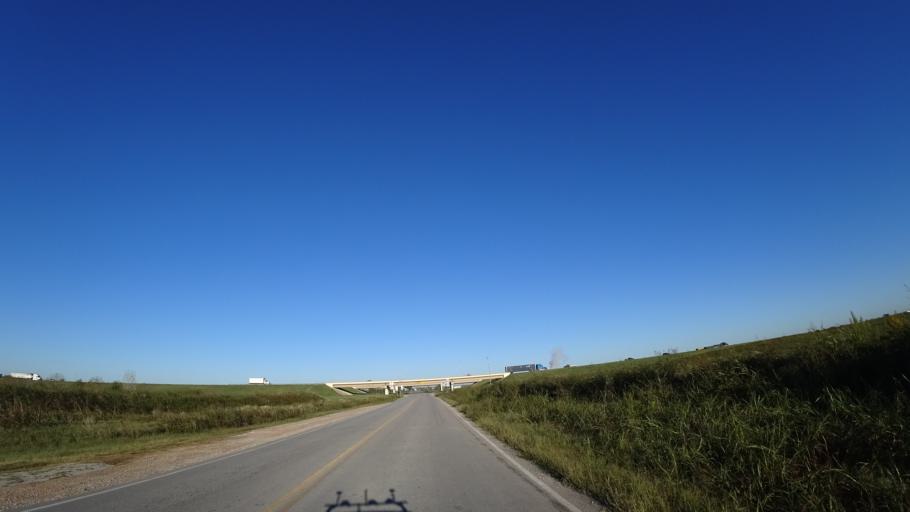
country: US
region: Texas
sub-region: Travis County
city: Hornsby Bend
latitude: 30.2278
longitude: -97.6178
